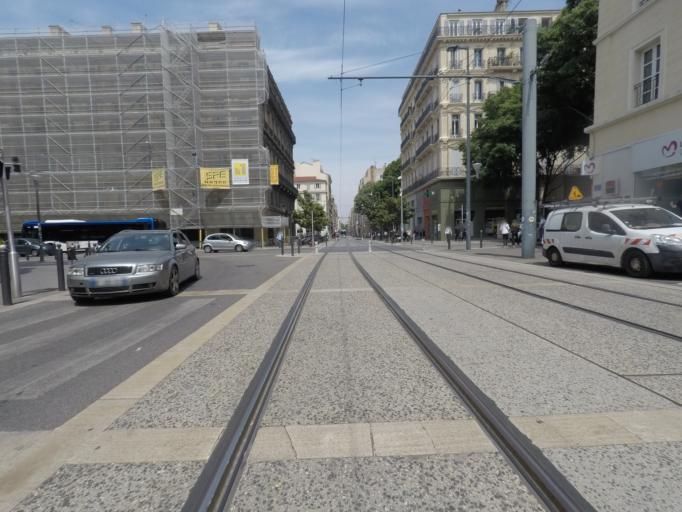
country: FR
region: Provence-Alpes-Cote d'Azur
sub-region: Departement des Bouches-du-Rhone
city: Marseille 06
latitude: 43.2906
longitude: 5.3811
